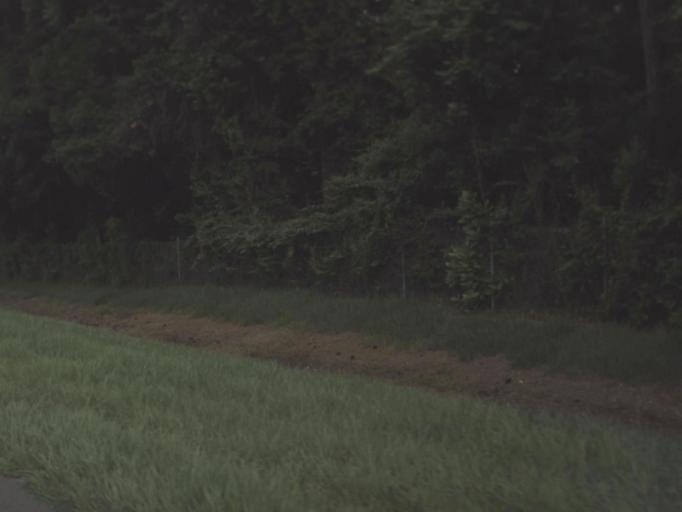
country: US
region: Florida
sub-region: Duval County
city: Jacksonville
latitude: 30.3572
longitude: -81.7089
